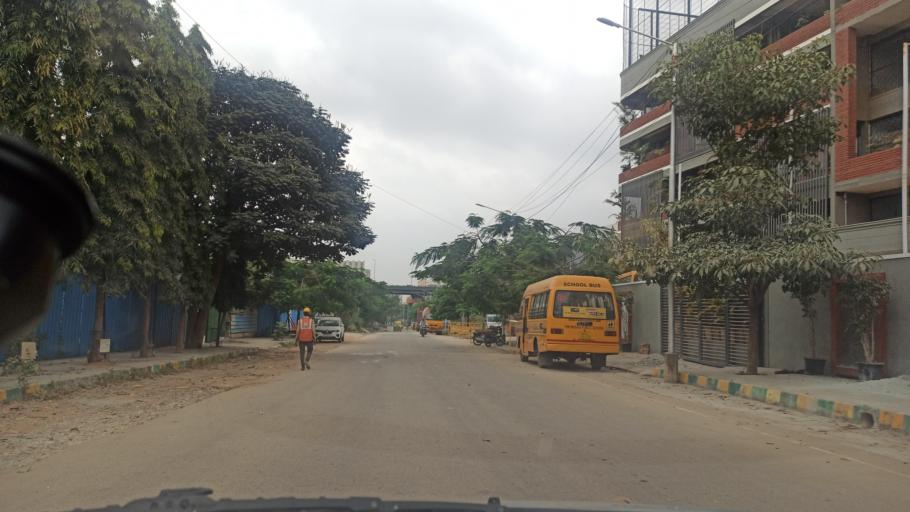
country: IN
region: Karnataka
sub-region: Bangalore Urban
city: Yelahanka
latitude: 13.0389
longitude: 77.6176
